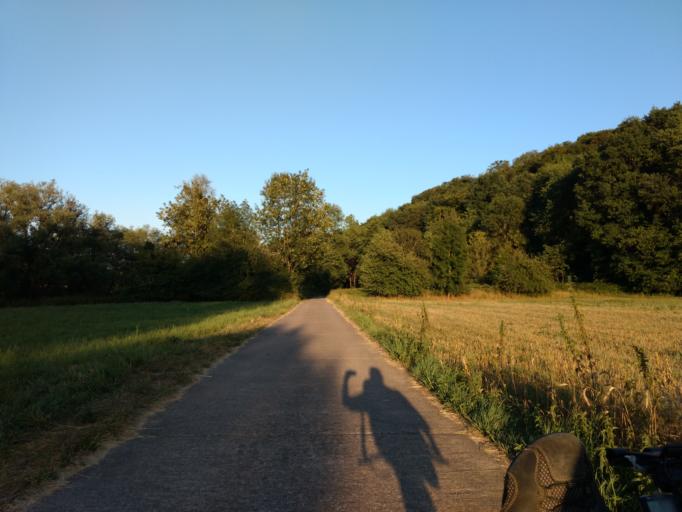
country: DE
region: Saarland
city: Rehlingen-Siersburg
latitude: 49.3638
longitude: 6.6473
